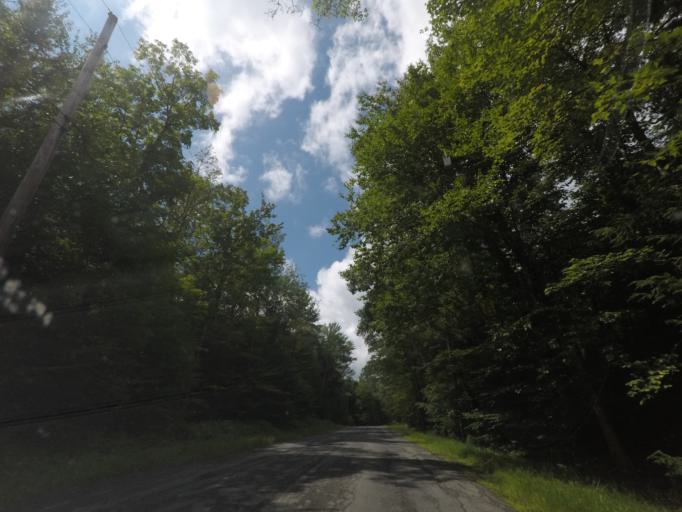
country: US
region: New York
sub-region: Rensselaer County
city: Averill Park
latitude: 42.6520
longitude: -73.4176
